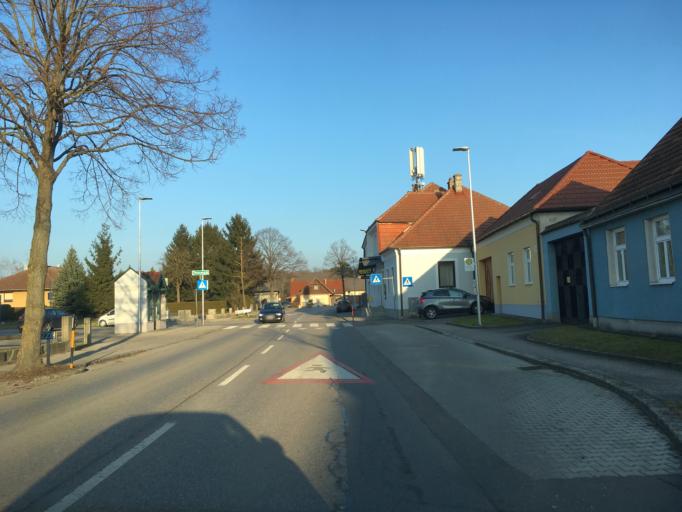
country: AT
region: Lower Austria
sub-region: Politischer Bezirk Tulln
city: Konigstetten
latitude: 48.3319
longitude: 16.1541
